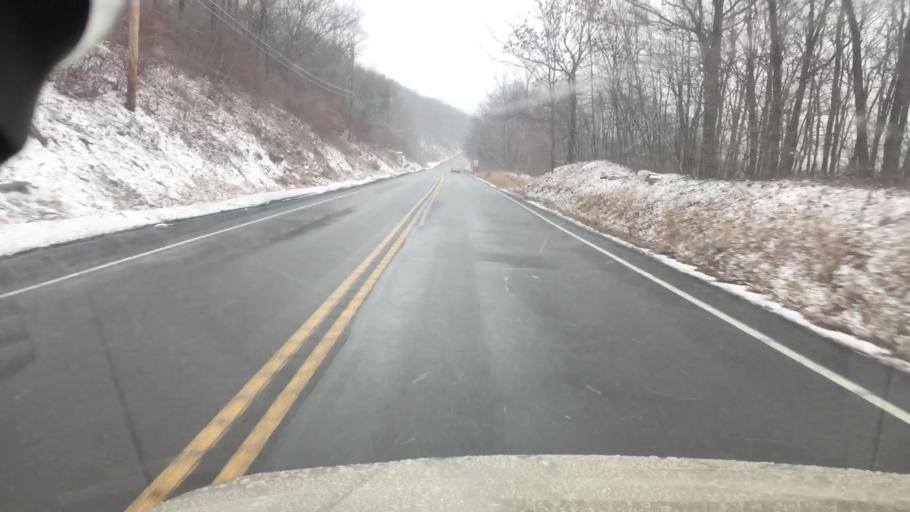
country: US
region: Pennsylvania
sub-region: Luzerne County
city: Conyngham
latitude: 41.0306
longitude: -76.0977
